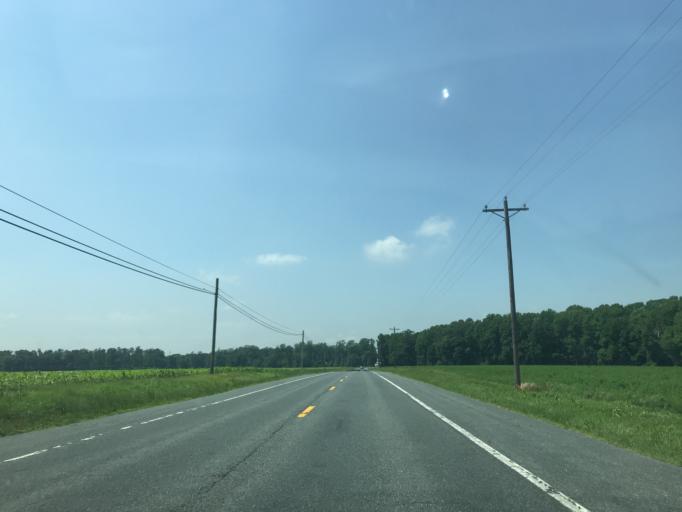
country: US
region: Maryland
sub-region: Caroline County
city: Federalsburg
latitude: 38.6593
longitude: -75.7311
